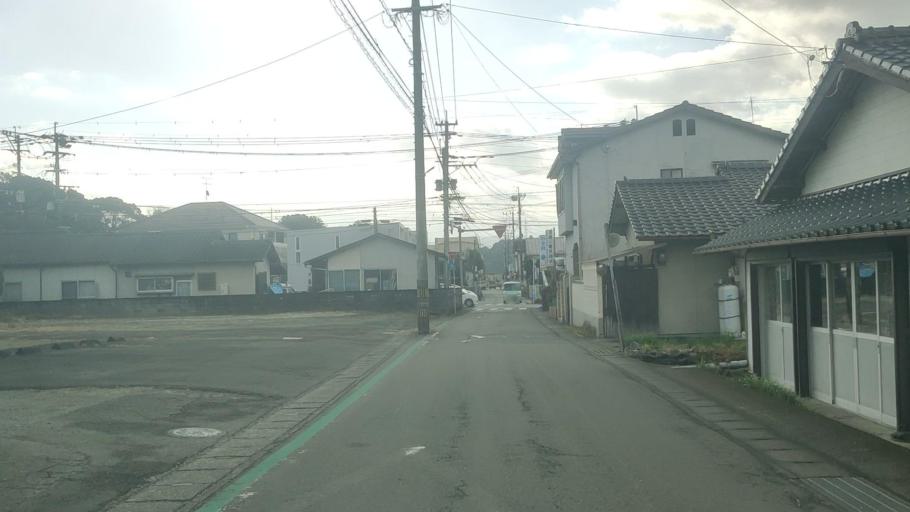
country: JP
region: Kumamoto
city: Hitoyoshi
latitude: 32.2200
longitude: 130.7716
